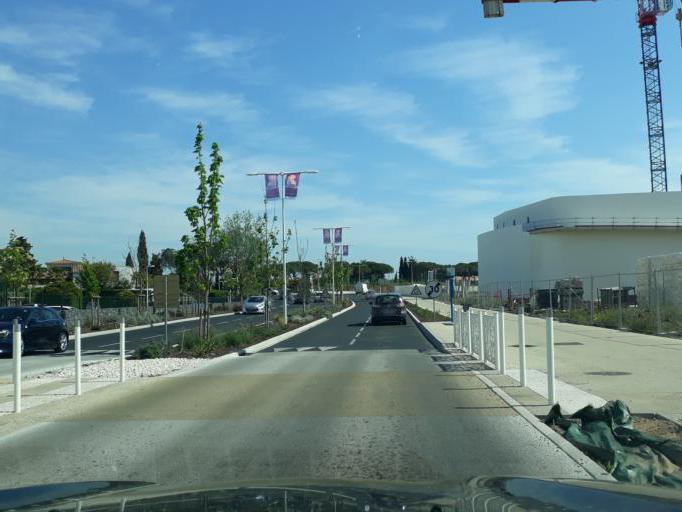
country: FR
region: Languedoc-Roussillon
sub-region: Departement de l'Herault
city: Le Cap d'Agde
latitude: 43.2873
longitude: 3.5067
